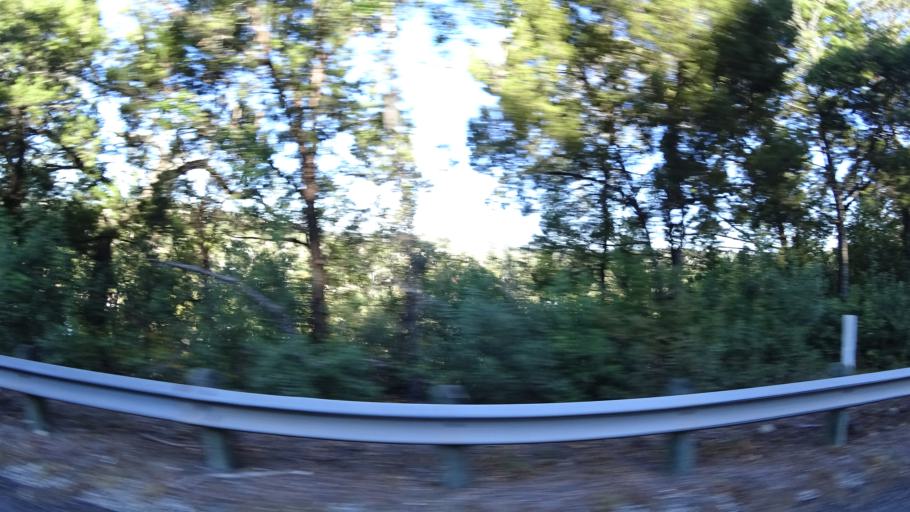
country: US
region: Texas
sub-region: Travis County
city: West Lake Hills
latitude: 30.3520
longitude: -97.7837
